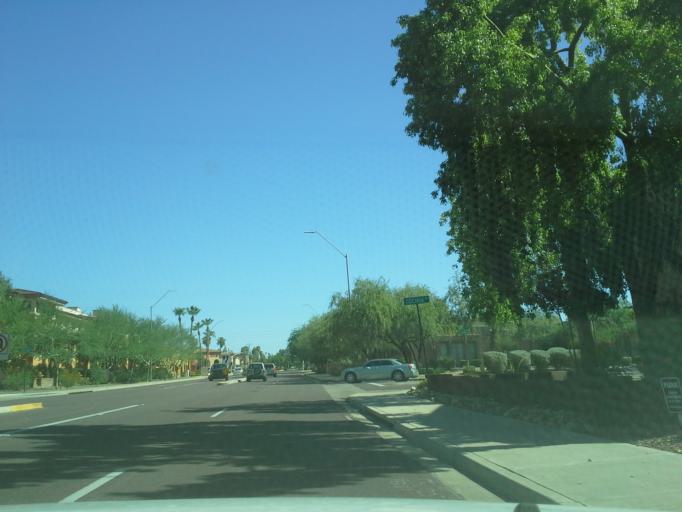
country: US
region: Arizona
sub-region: Maricopa County
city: Paradise Valley
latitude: 33.5799
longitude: -111.9303
